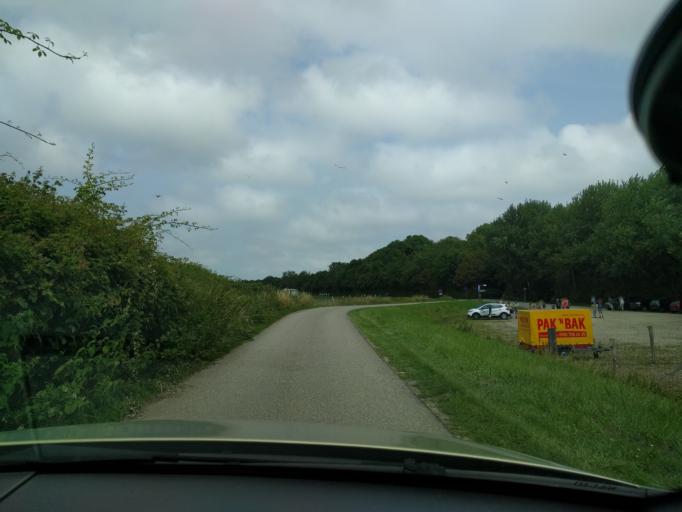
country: NL
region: Zeeland
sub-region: Gemeente Veere
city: Veere
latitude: 51.5332
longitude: 3.6777
